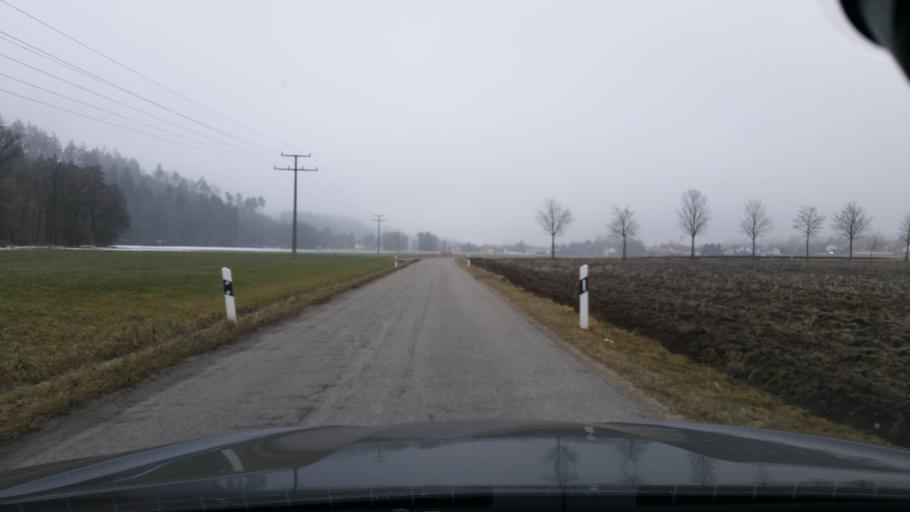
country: DE
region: Bavaria
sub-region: Lower Bavaria
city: Weihmichl
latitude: 48.5660
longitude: 12.0867
